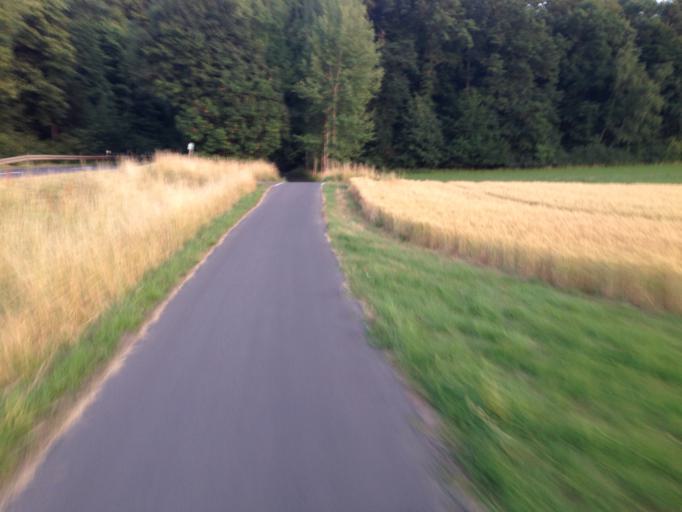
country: DE
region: Hesse
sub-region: Regierungsbezirk Giessen
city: Grossen Buseck
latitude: 50.5696
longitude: 8.7679
